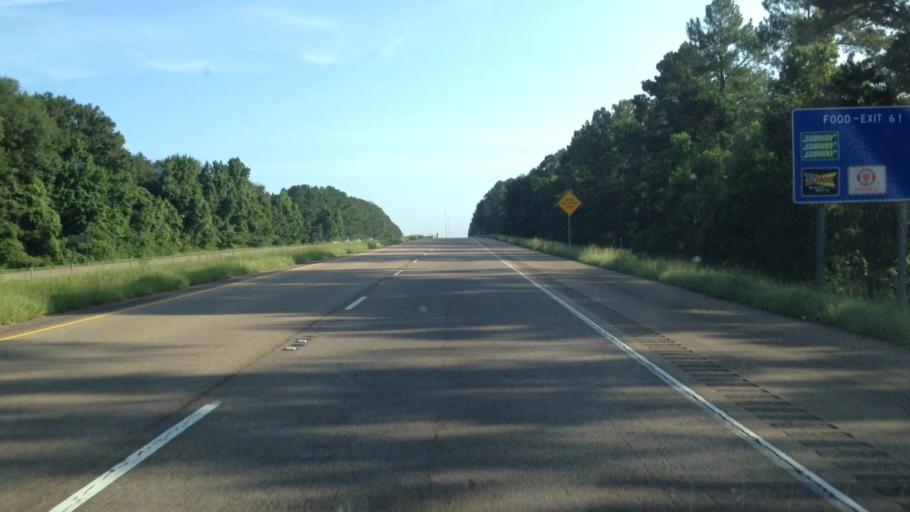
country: US
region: Louisiana
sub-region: Tangipahoa Parish
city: Kentwood
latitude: 30.9222
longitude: -90.5242
